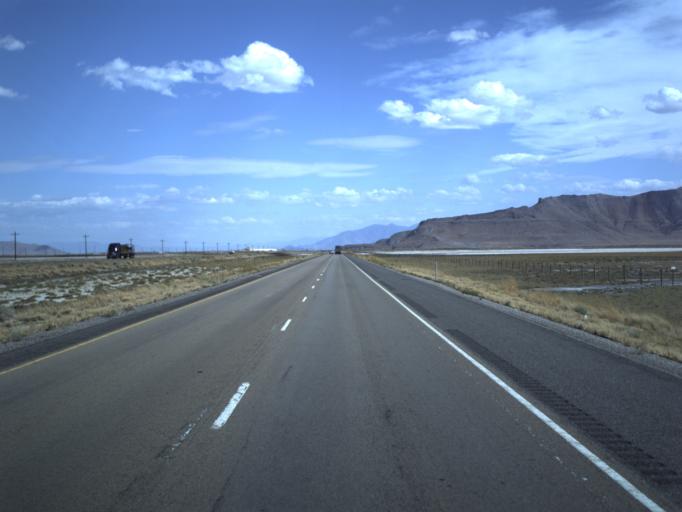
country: US
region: Utah
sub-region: Tooele County
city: Grantsville
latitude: 40.7518
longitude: -112.7150
